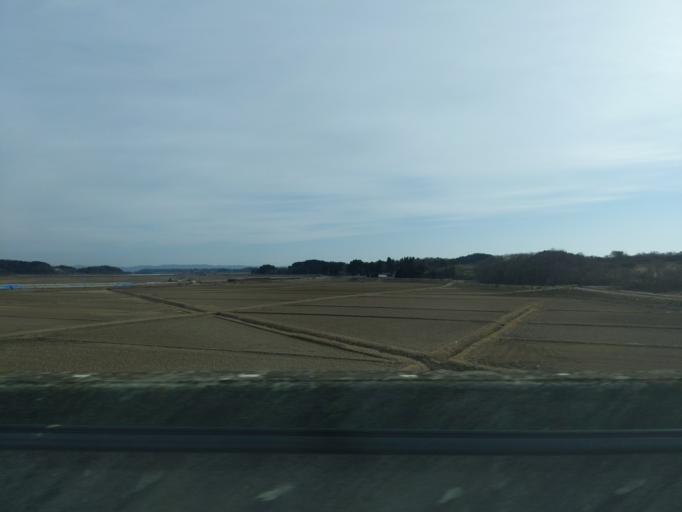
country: JP
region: Miyagi
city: Kogota
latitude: 38.7245
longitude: 141.0579
